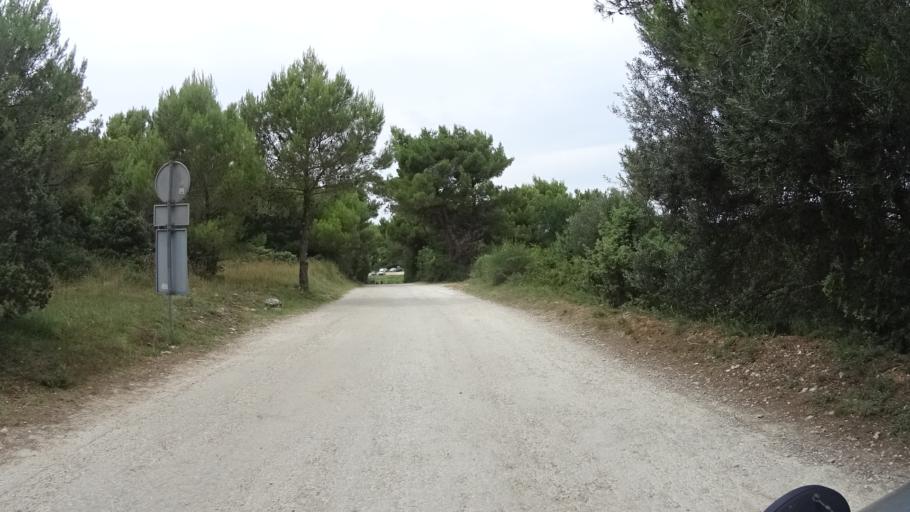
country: HR
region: Istarska
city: Medulin
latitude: 44.7967
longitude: 13.9077
